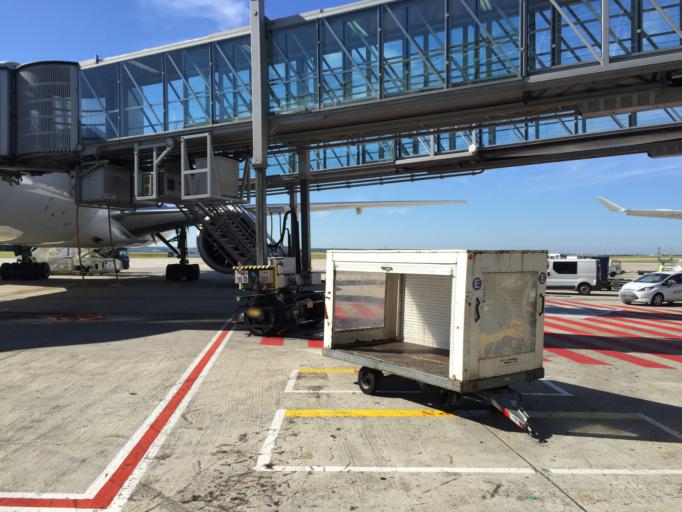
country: FR
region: Ile-de-France
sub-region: Departement de Seine-et-Marne
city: Mitry-Mory
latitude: 49.0019
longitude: 2.5800
